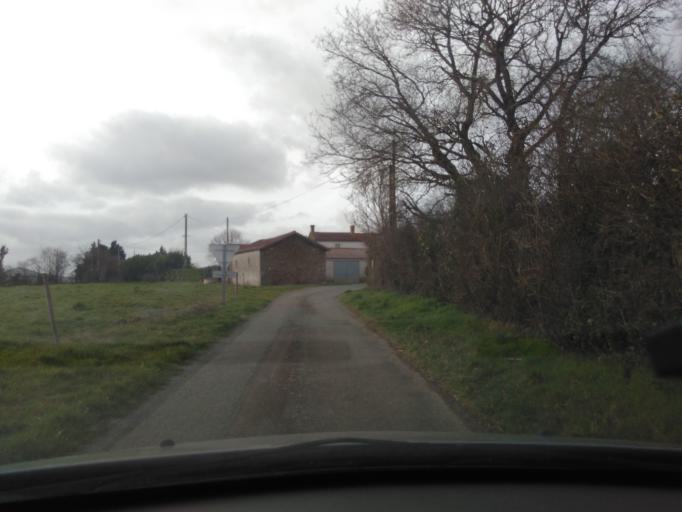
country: FR
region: Pays de la Loire
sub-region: Departement de la Vendee
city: Sainte-Cecile
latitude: 46.7081
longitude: -1.1194
